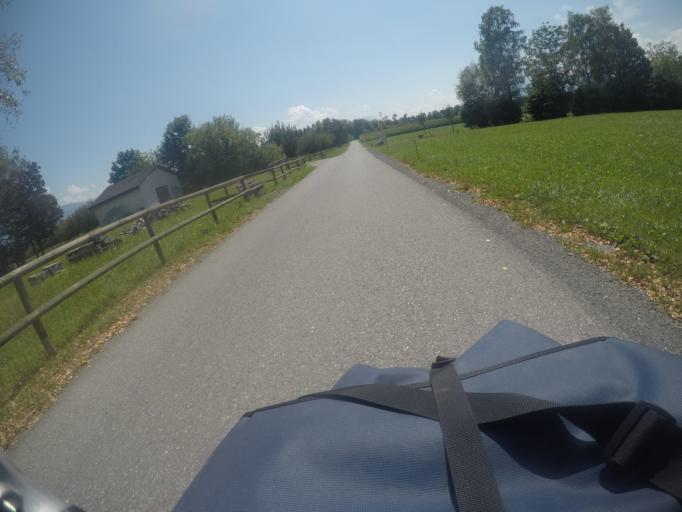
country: CH
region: Saint Gallen
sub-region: Wahlkreis Rheintal
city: Rebstein
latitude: 47.3884
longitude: 9.5718
